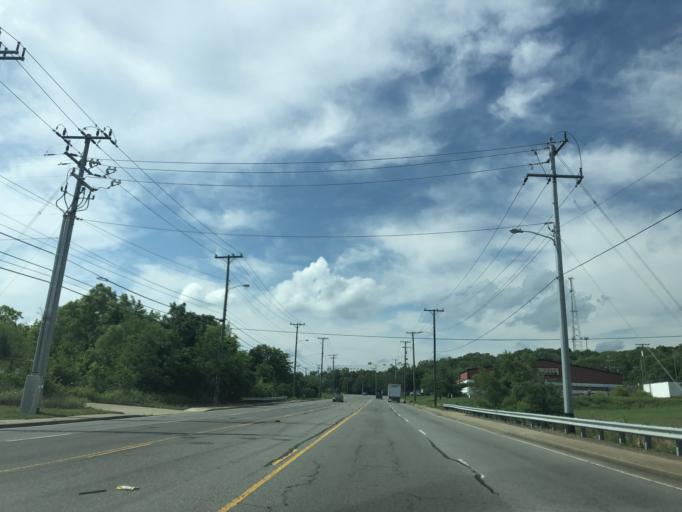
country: US
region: Tennessee
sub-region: Davidson County
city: Nashville
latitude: 36.2124
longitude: -86.7789
